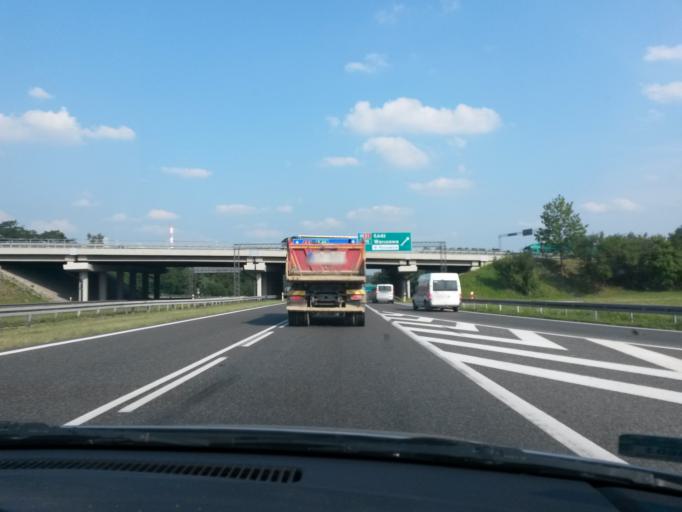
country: PL
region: Silesian Voivodeship
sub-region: Myslowice
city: Myslowice
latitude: 50.2080
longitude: 19.1651
